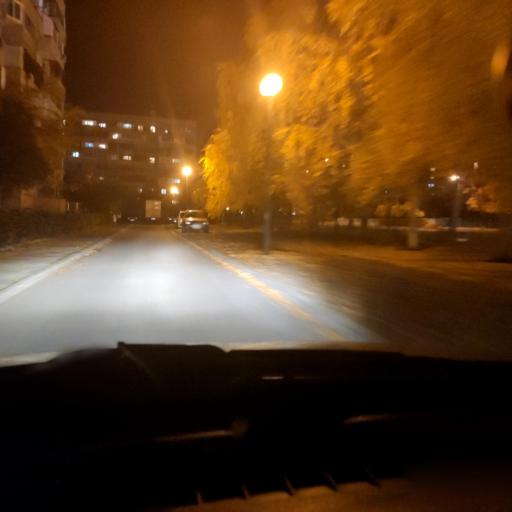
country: RU
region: Samara
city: Tol'yatti
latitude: 53.5378
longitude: 49.3328
